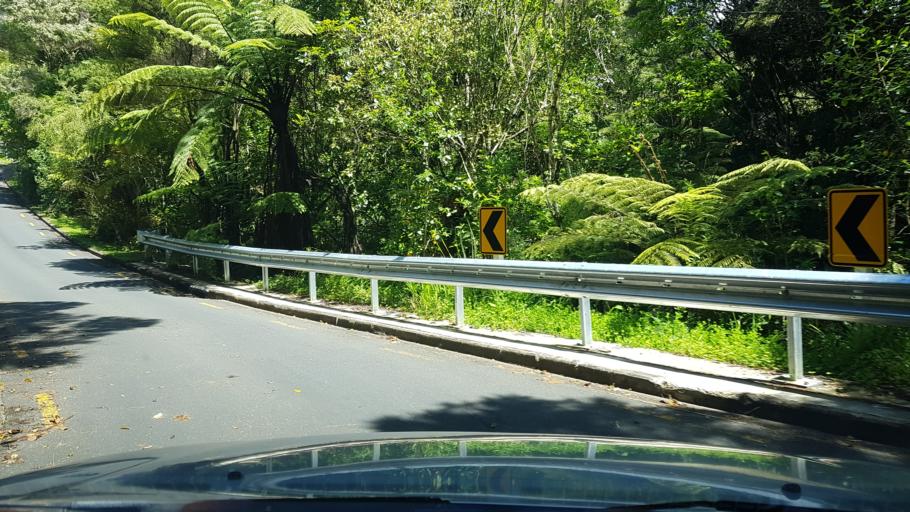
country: NZ
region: Auckland
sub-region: Auckland
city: North Shore
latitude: -36.8118
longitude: 174.7045
